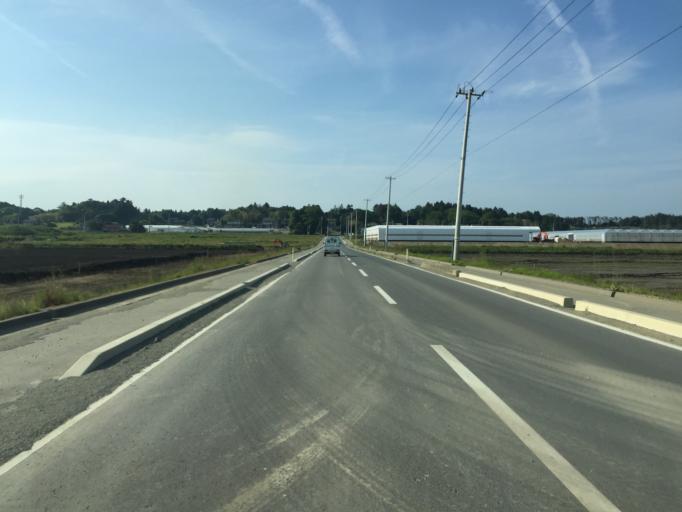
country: JP
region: Fukushima
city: Namie
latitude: 37.7034
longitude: 141.0057
